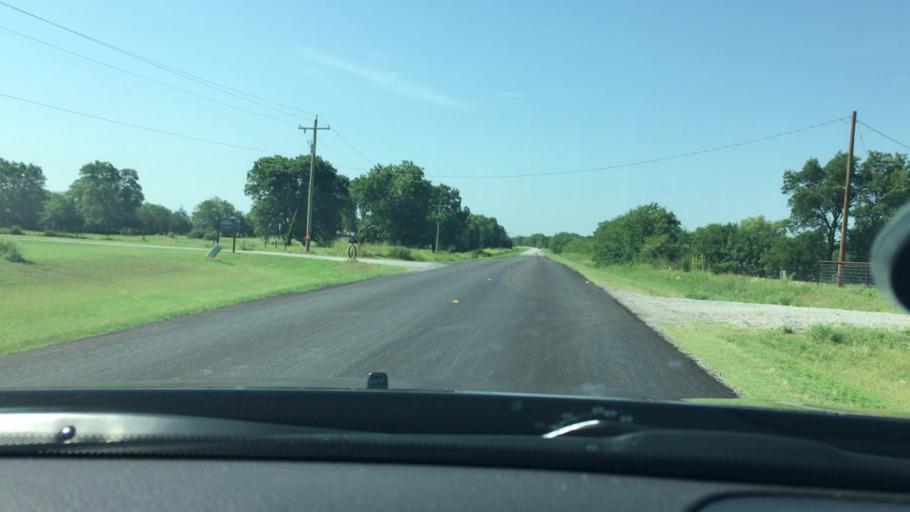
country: US
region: Oklahoma
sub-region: Coal County
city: Coalgate
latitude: 34.3577
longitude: -96.4246
